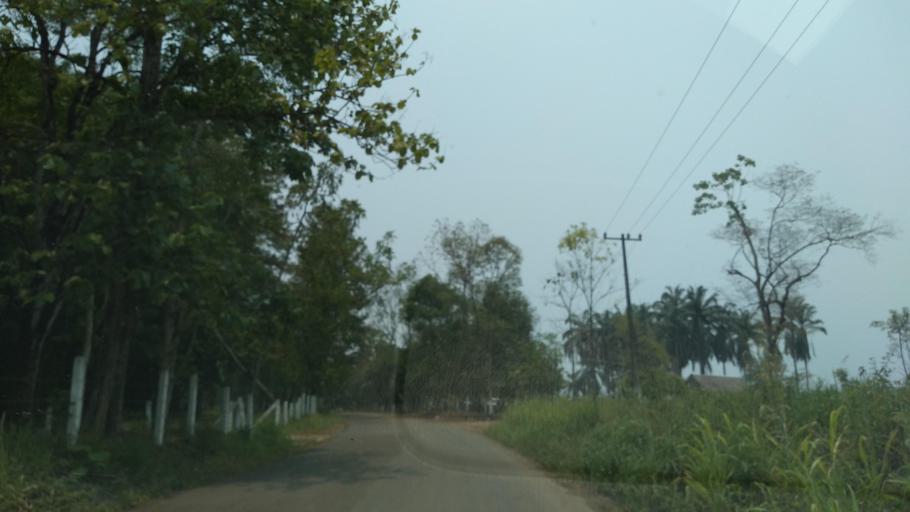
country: MX
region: Veracruz
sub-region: Tezonapa
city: Laguna Chica (Pueblo Nuevo)
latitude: 18.5136
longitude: -96.7586
